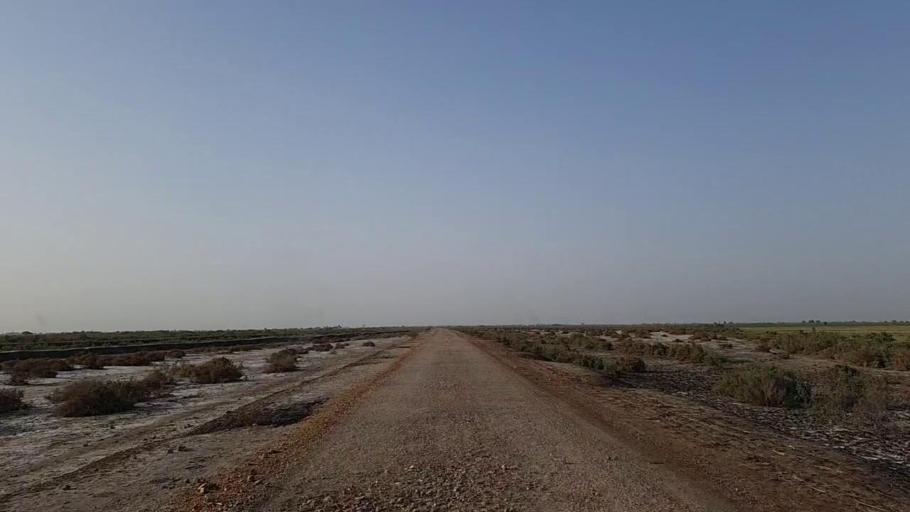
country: PK
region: Sindh
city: Jati
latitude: 24.3531
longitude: 68.1488
